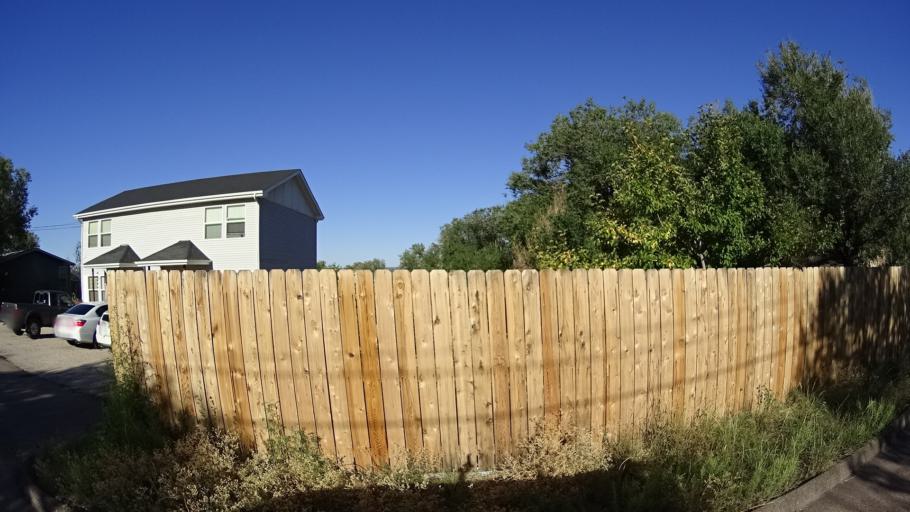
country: US
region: Colorado
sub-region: El Paso County
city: Manitou Springs
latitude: 38.8337
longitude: -104.8750
